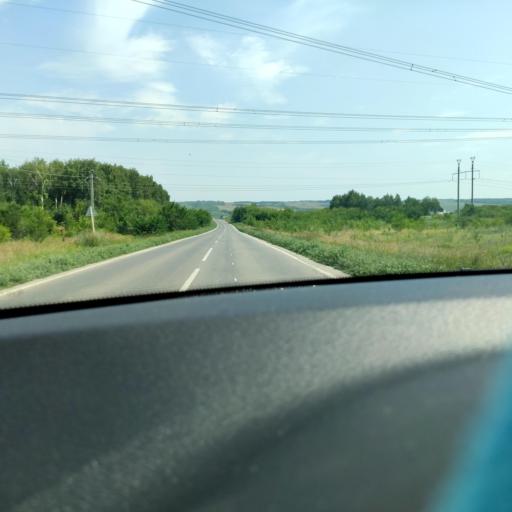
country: RU
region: Samara
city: Petra-Dubrava
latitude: 53.3465
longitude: 50.5076
